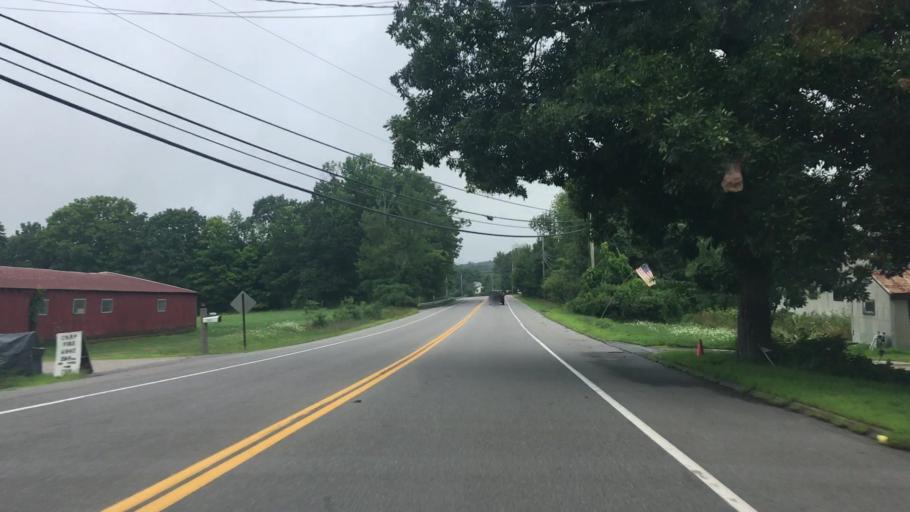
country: US
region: Maine
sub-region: York County
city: Lebanon
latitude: 43.4238
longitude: -70.8252
